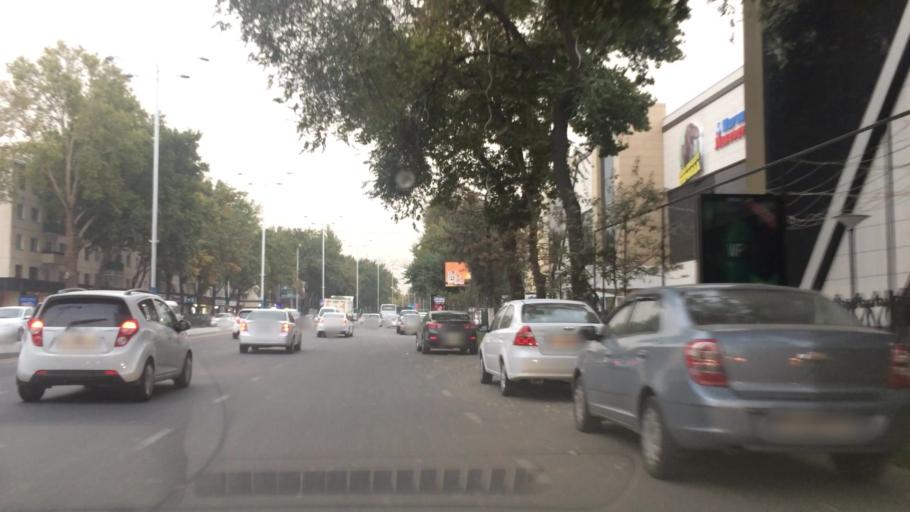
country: UZ
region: Toshkent Shahri
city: Tashkent
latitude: 41.2976
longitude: 69.2499
